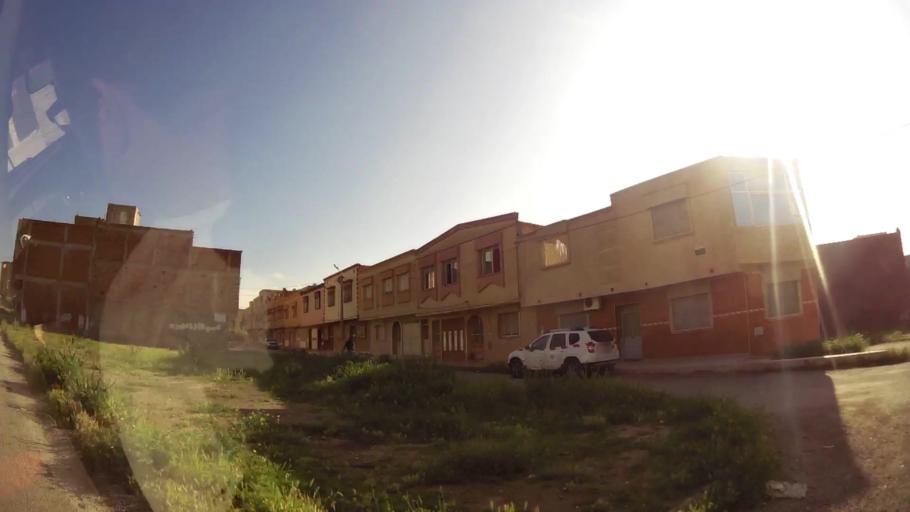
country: MA
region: Oriental
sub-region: Oujda-Angad
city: Oujda
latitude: 34.6738
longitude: -1.9440
